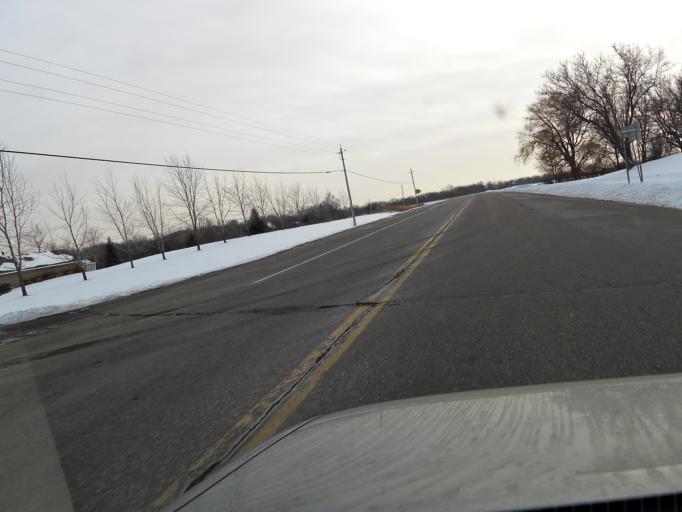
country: US
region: Minnesota
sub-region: Scott County
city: Shakopee
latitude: 44.7370
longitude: -93.4995
